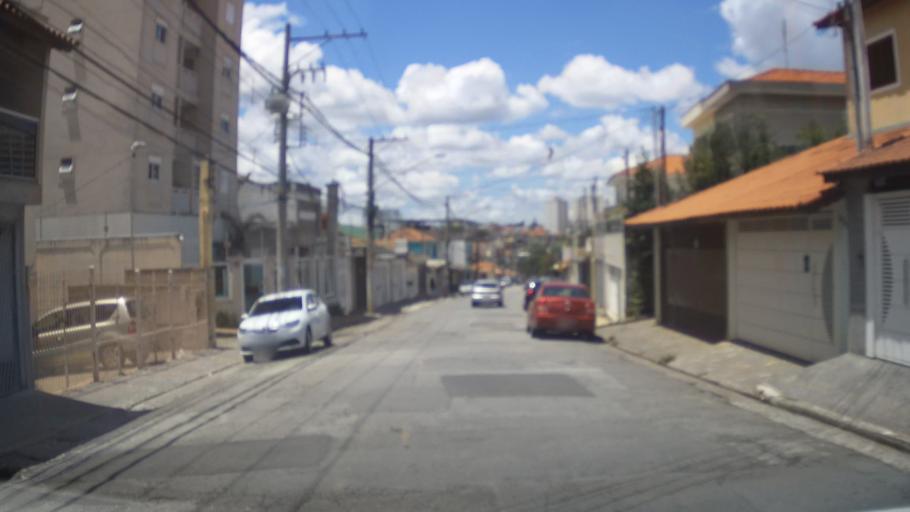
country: BR
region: Sao Paulo
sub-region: Guarulhos
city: Guarulhos
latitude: -23.4485
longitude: -46.5403
